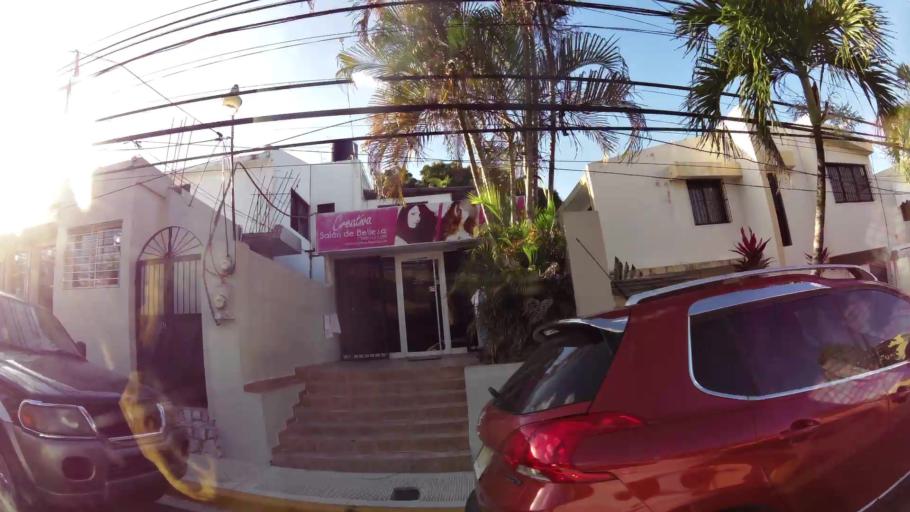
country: DO
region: Nacional
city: Santo Domingo
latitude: 18.4954
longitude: -69.9716
